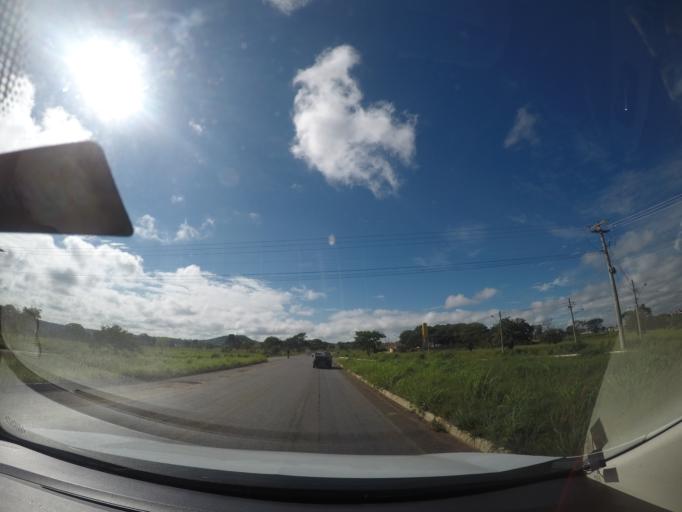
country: BR
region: Goias
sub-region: Senador Canedo
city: Senador Canedo
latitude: -16.6703
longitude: -49.1465
